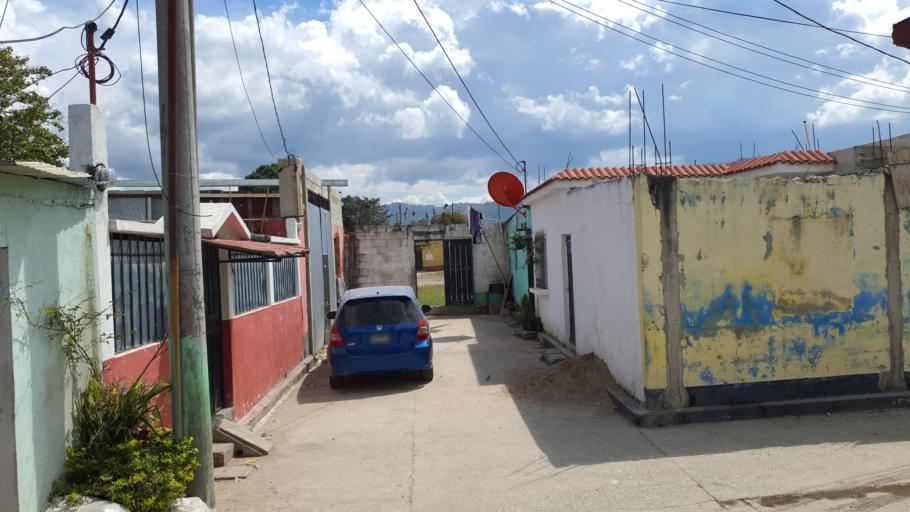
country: GT
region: Guatemala
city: Villa Canales
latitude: 14.4573
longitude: -90.5569
